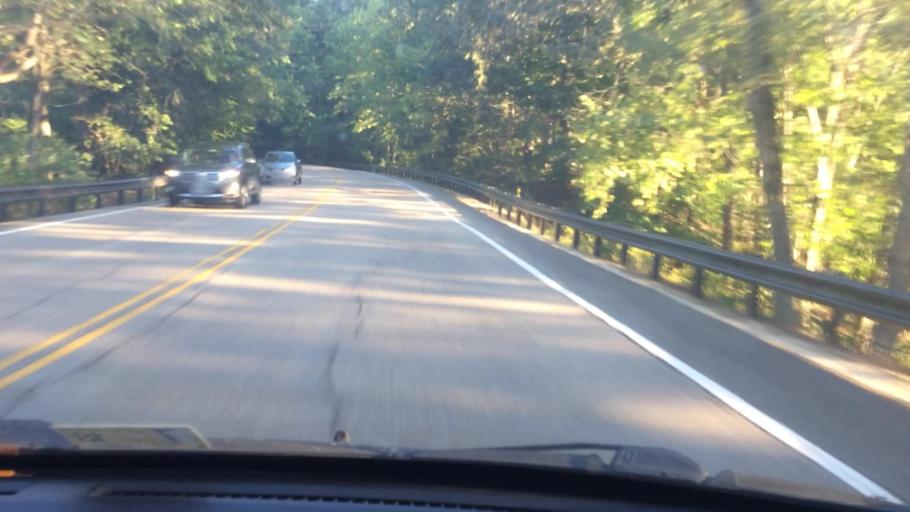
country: US
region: Virginia
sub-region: City of Williamsburg
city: Williamsburg
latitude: 37.2517
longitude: -76.7094
